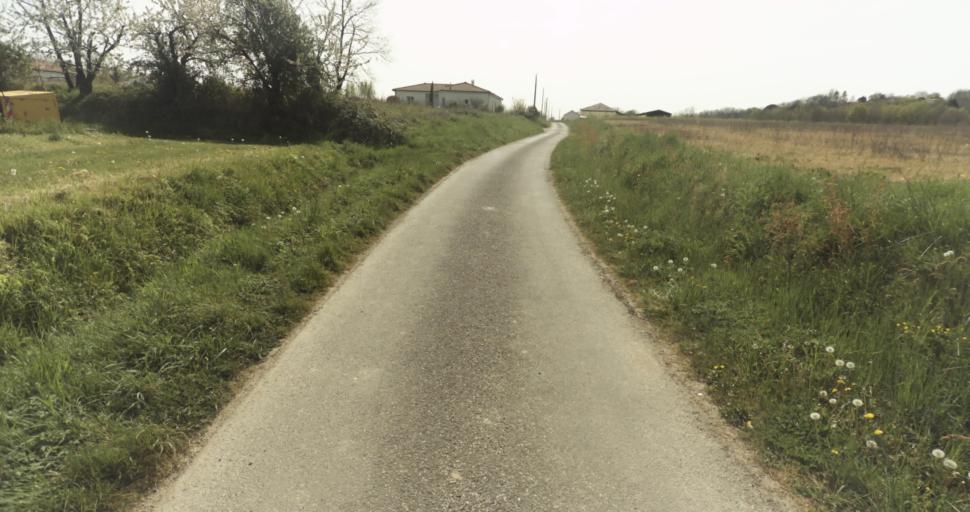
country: FR
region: Midi-Pyrenees
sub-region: Departement du Tarn-et-Garonne
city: Moissac
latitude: 44.1288
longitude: 1.1541
